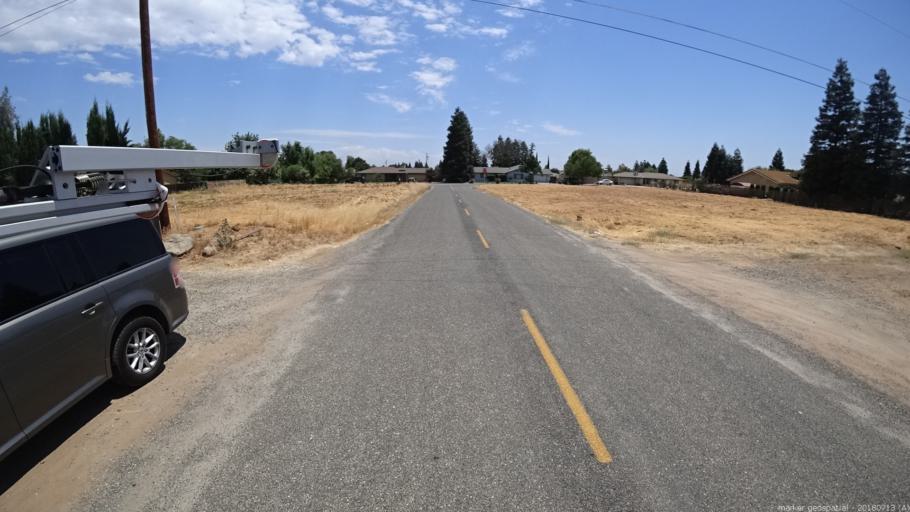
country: US
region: California
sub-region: Madera County
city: Madera Acres
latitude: 36.9951
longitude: -120.0775
